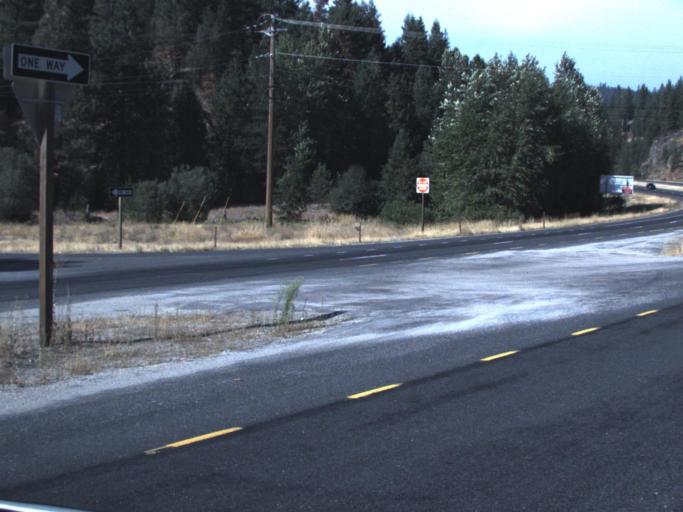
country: US
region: Washington
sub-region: Spokane County
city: Deer Park
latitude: 48.0808
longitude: -117.3238
